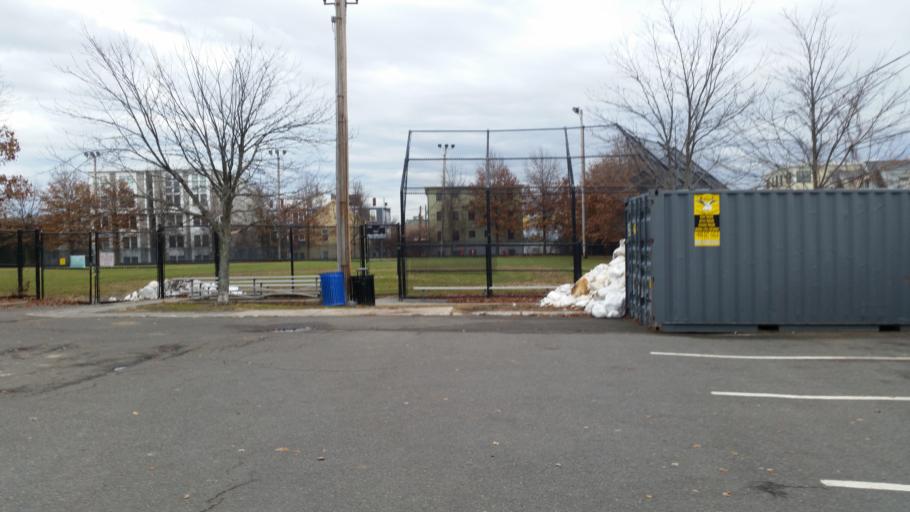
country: US
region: Massachusetts
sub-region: Middlesex County
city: Cambridge
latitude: 42.3824
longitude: -71.1086
